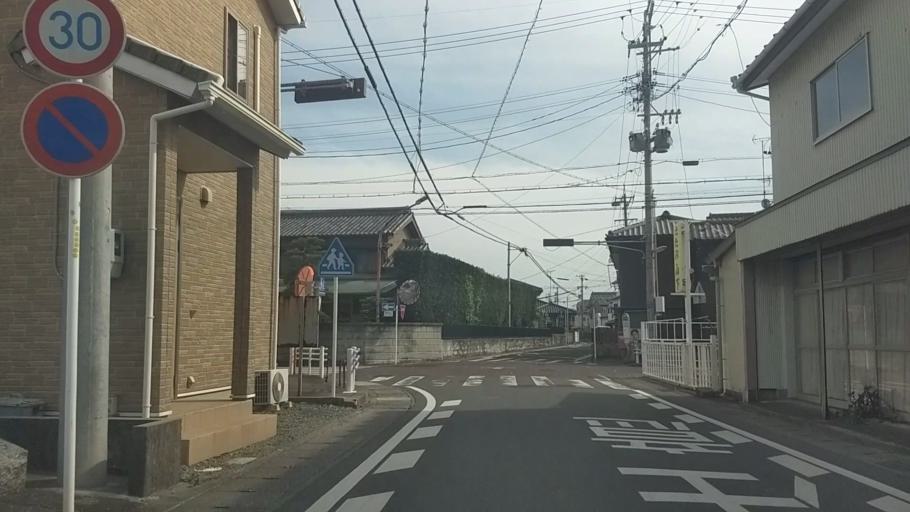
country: JP
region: Shizuoka
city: Kosai-shi
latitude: 34.7023
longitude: 137.6293
